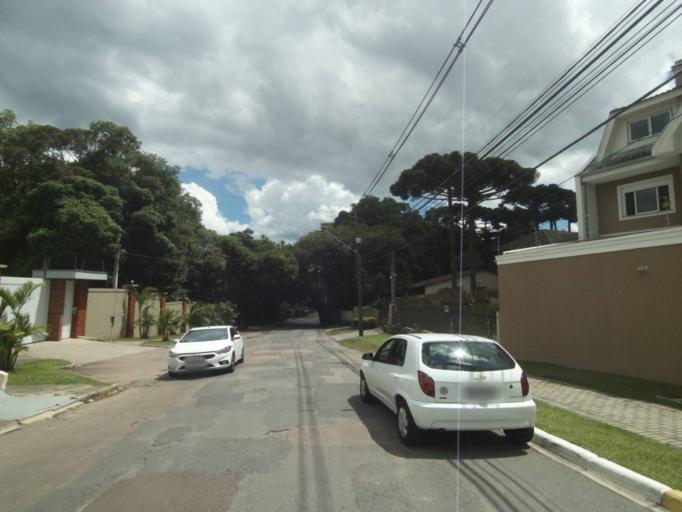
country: BR
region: Parana
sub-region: Curitiba
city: Curitiba
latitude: -25.4340
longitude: -49.3393
